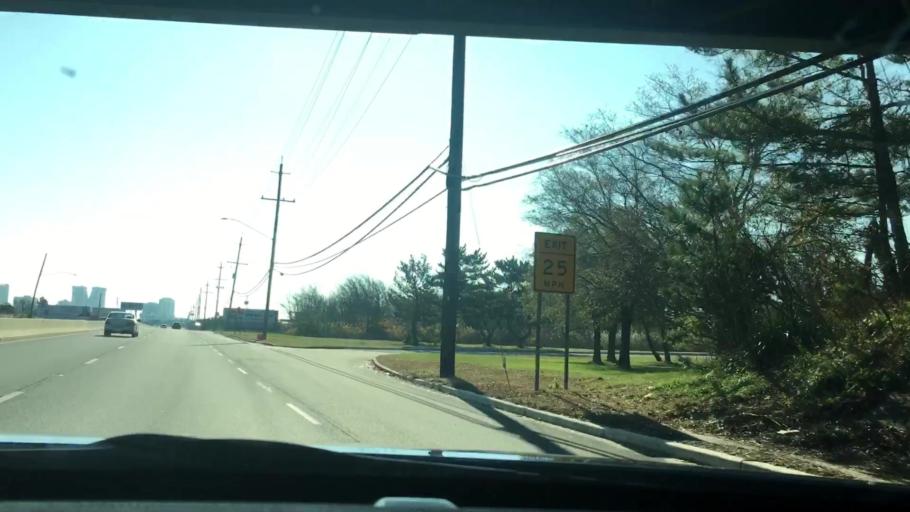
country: US
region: New Jersey
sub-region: Atlantic County
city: Ventnor City
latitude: 39.3676
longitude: -74.4733
